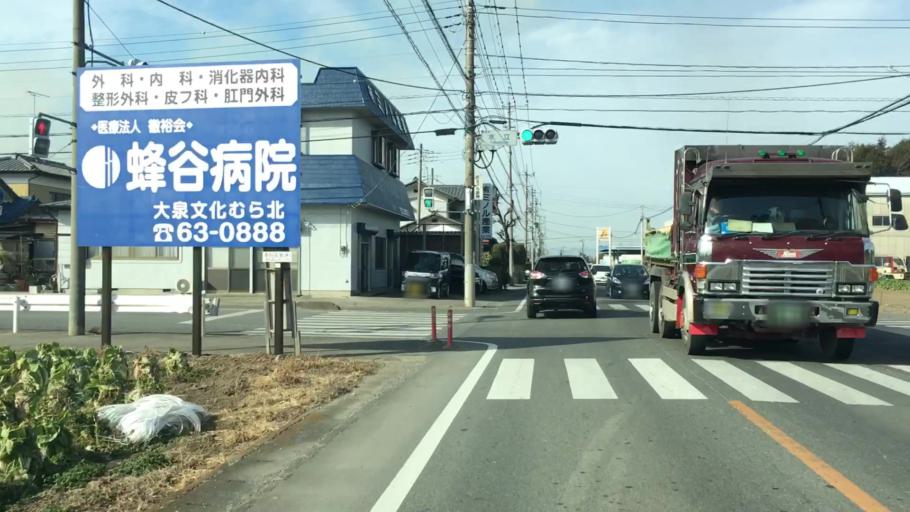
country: JP
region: Saitama
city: Menuma
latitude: 36.2417
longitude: 139.4517
